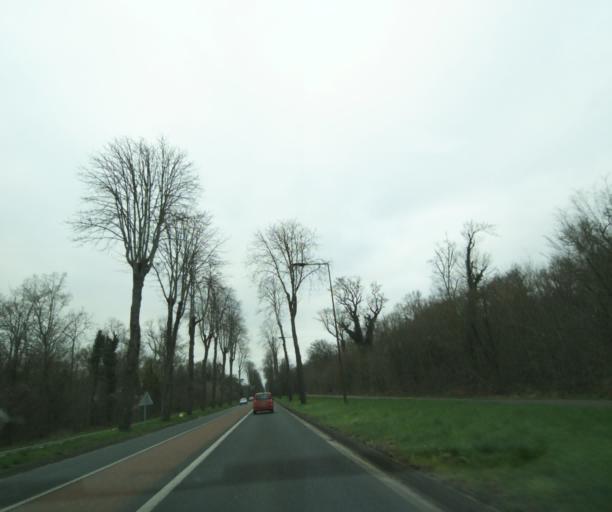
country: FR
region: Ile-de-France
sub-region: Departement des Yvelines
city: Poissy
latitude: 48.9166
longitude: 2.0647
